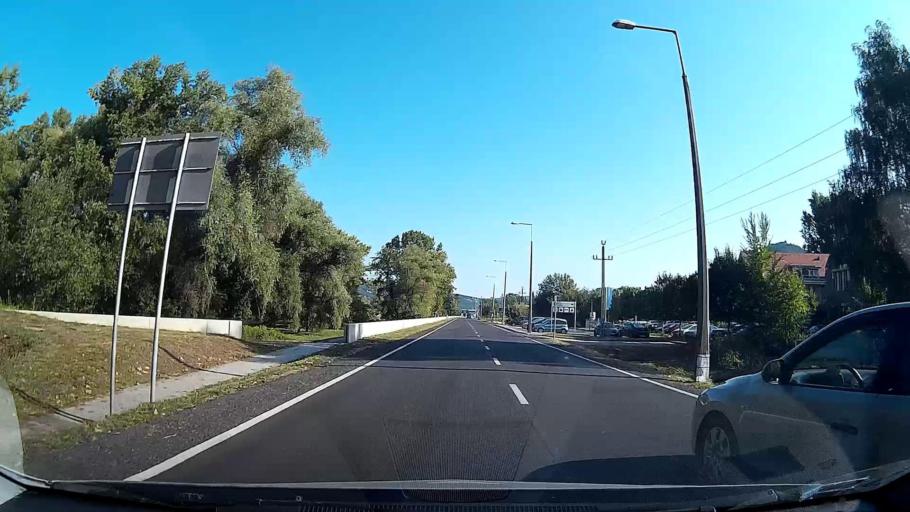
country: HU
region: Pest
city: Visegrad
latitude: 47.7820
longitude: 18.9671
